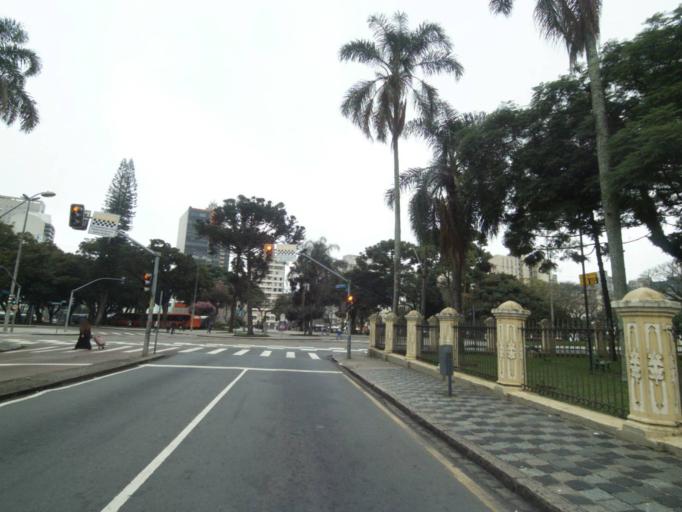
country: BR
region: Parana
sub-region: Curitiba
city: Curitiba
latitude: -25.4369
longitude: -49.2733
